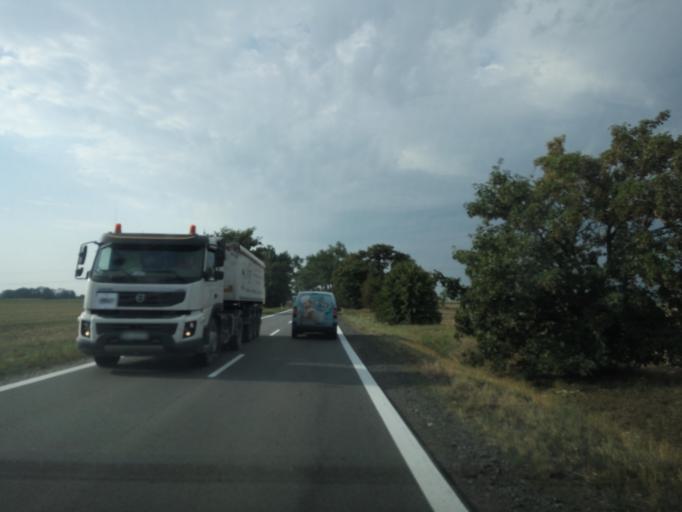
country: PL
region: Lower Silesian Voivodeship
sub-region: Powiat wroclawski
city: Zerniki Wroclawskie
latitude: 51.0106
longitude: 17.0647
